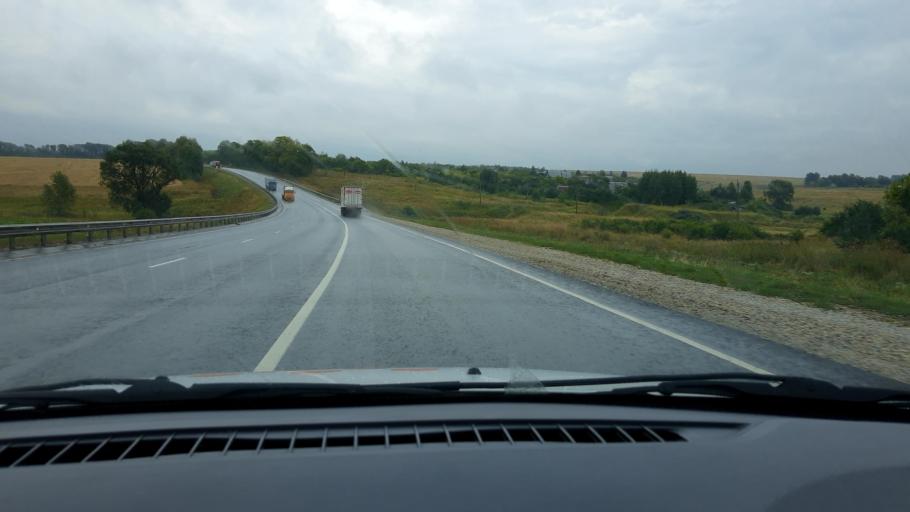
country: RU
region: Chuvashia
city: Tsivil'sk
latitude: 55.7911
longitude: 47.6749
